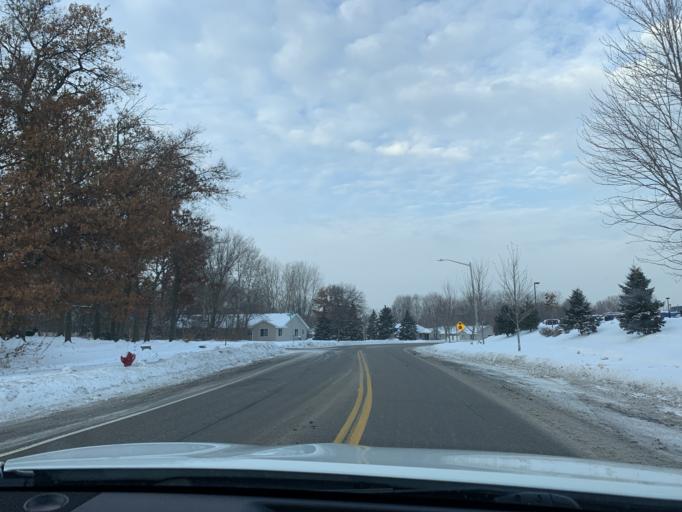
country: US
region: Minnesota
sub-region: Anoka County
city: Coon Rapids
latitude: 45.1611
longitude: -93.2868
